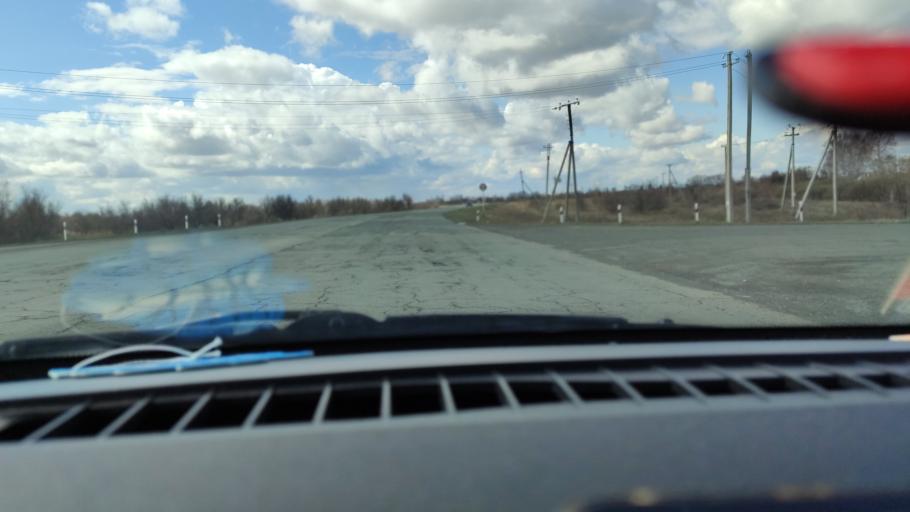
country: RU
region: Samara
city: Tol'yatti
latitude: 53.7190
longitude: 49.4274
